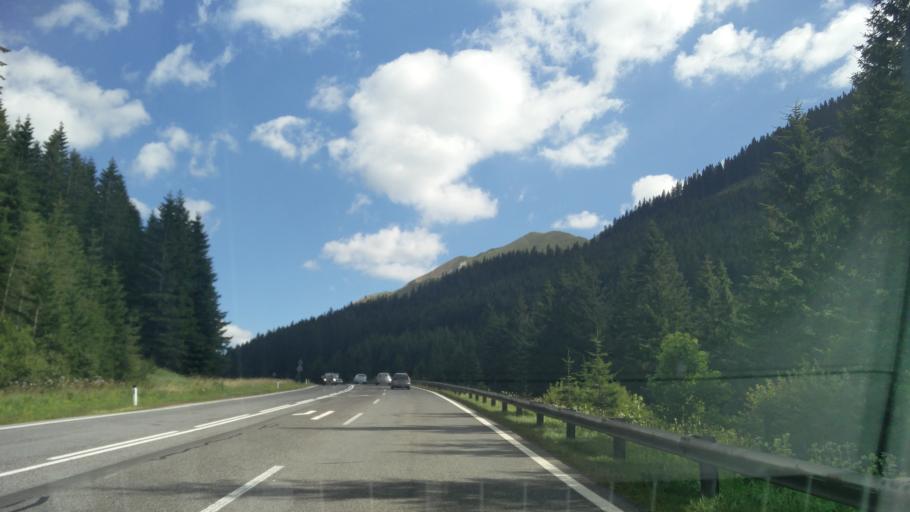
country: AT
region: Styria
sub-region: Politischer Bezirk Leoben
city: Eisenerz
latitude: 47.5268
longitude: 14.9448
